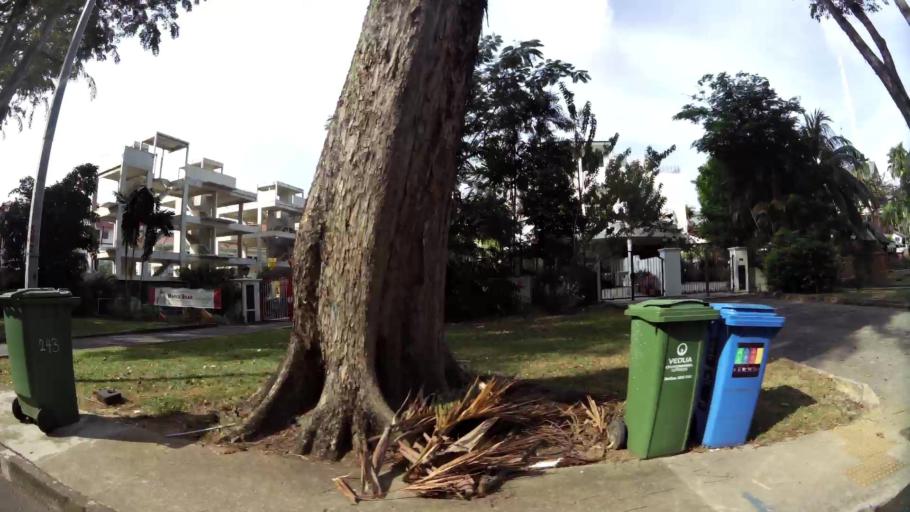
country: SG
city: Singapore
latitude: 1.2806
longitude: 103.7850
